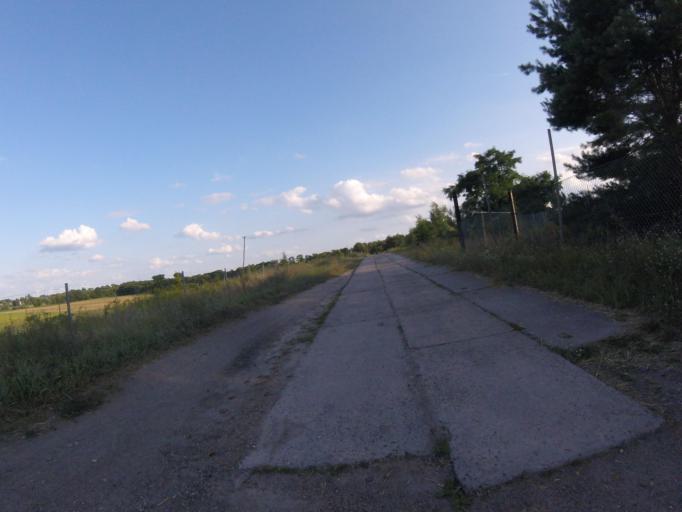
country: DE
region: Brandenburg
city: Mittenwalde
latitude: 52.2775
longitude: 13.5155
